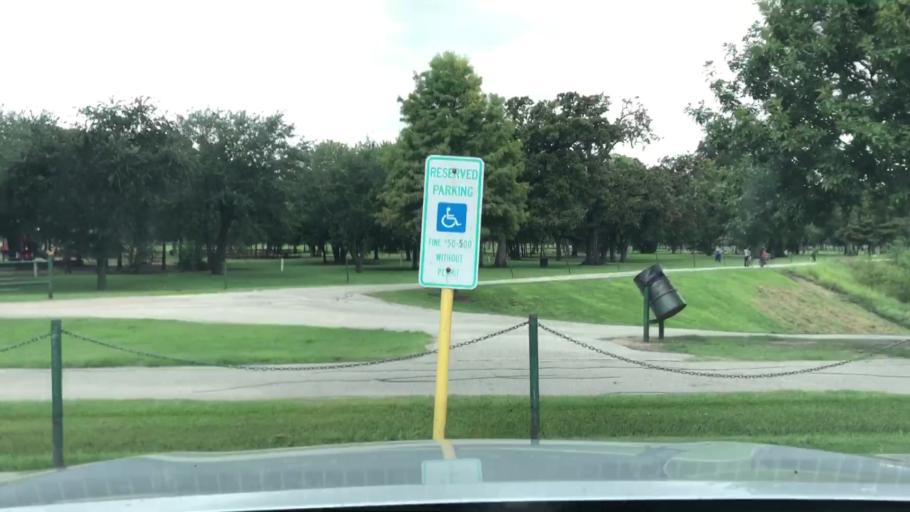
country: US
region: Texas
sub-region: Fort Bend County
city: Meadows Place
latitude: 29.6964
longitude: -95.5579
